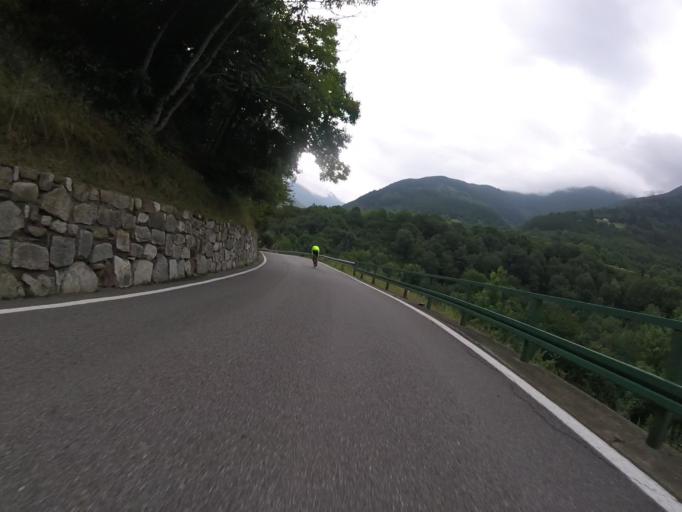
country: IT
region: Lombardy
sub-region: Provincia di Brescia
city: Incudine
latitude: 46.2139
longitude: 10.3509
